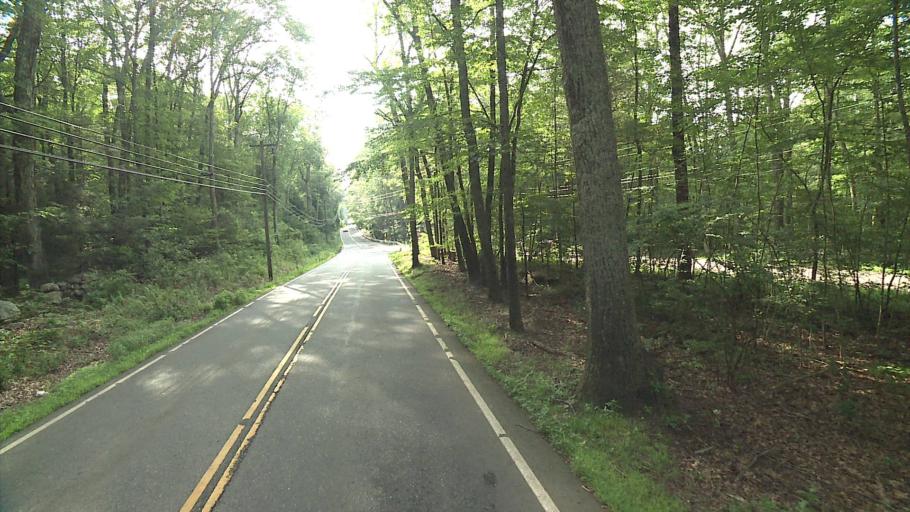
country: US
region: Massachusetts
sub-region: Worcester County
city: Southbridge
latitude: 41.9737
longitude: -72.0677
